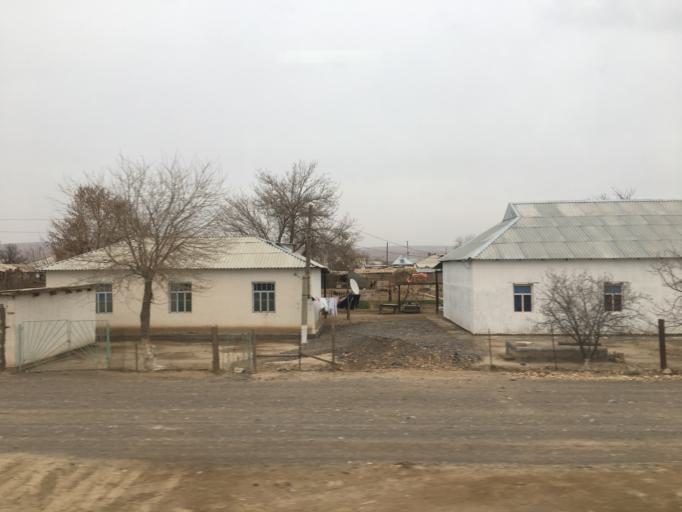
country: TM
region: Mary
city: Yoloeten
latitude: 36.5347
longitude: 62.5541
